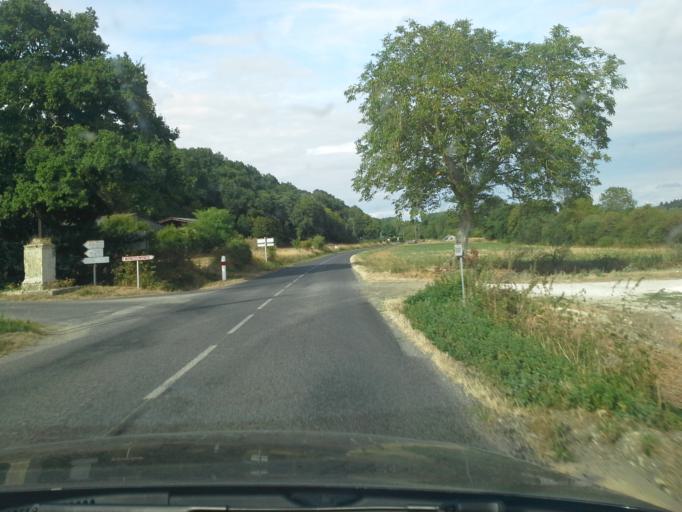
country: FR
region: Centre
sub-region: Departement d'Indre-et-Loire
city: Reugny
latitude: 47.4953
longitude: 0.8948
